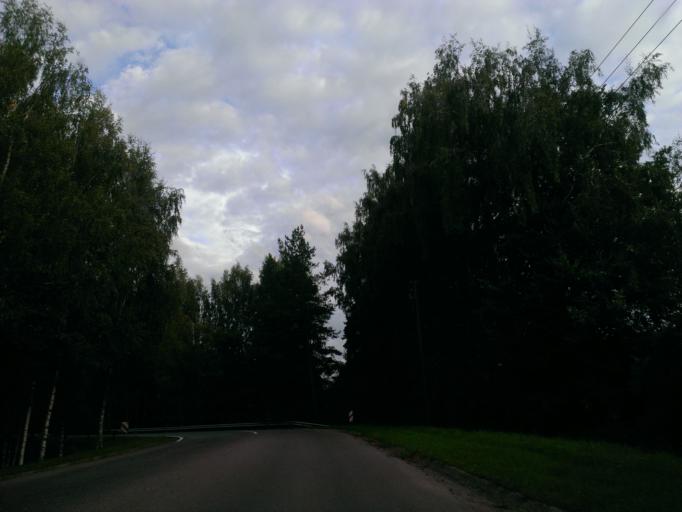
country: LV
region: Ikskile
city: Ikskile
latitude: 56.8361
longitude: 24.4972
